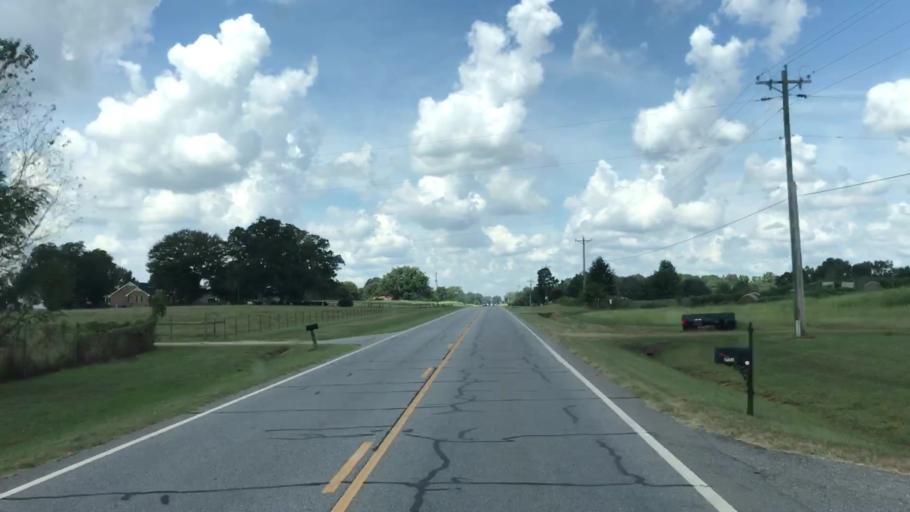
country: US
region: Georgia
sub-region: Oconee County
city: Watkinsville
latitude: 33.8238
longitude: -83.3701
